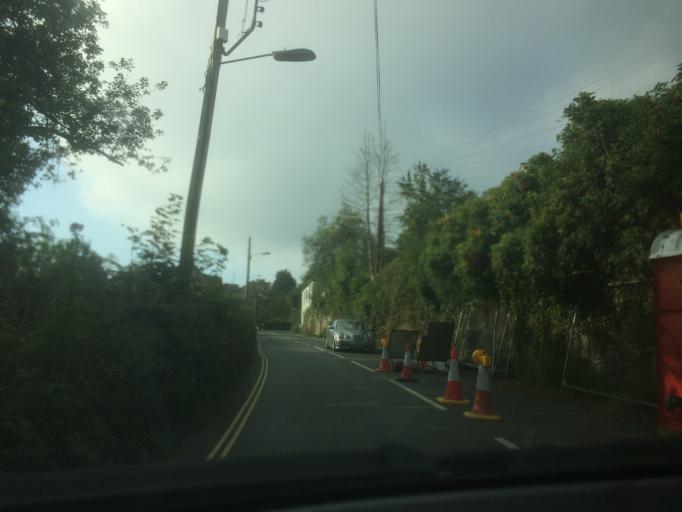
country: GB
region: England
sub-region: Cornwall
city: Gunnislake
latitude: 50.5262
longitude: -4.2127
